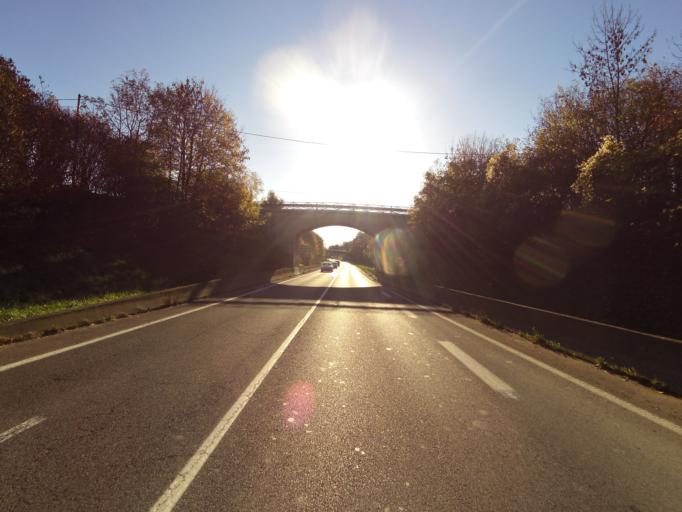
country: FR
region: Champagne-Ardenne
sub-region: Departement de l'Aube
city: Breviandes
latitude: 48.2597
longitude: 4.0967
